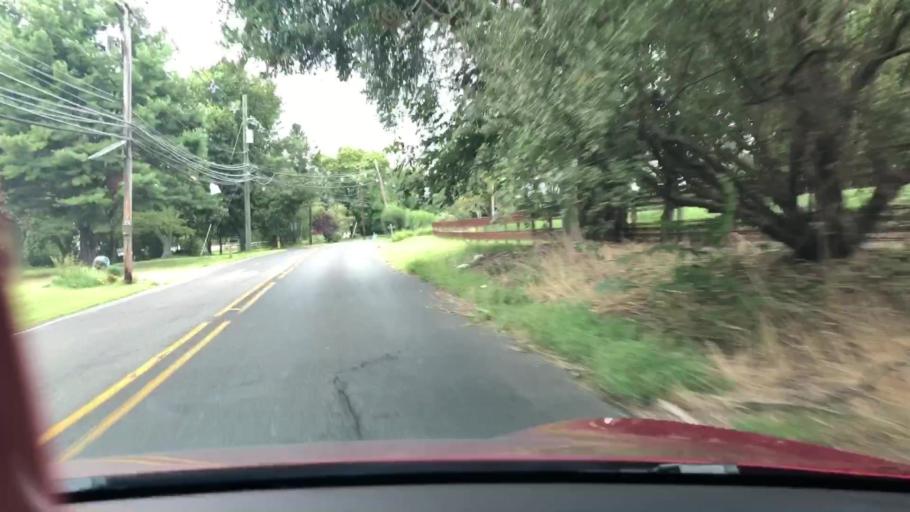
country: US
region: New Jersey
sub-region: Monmouth County
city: Allentown
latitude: 40.1837
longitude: -74.5918
